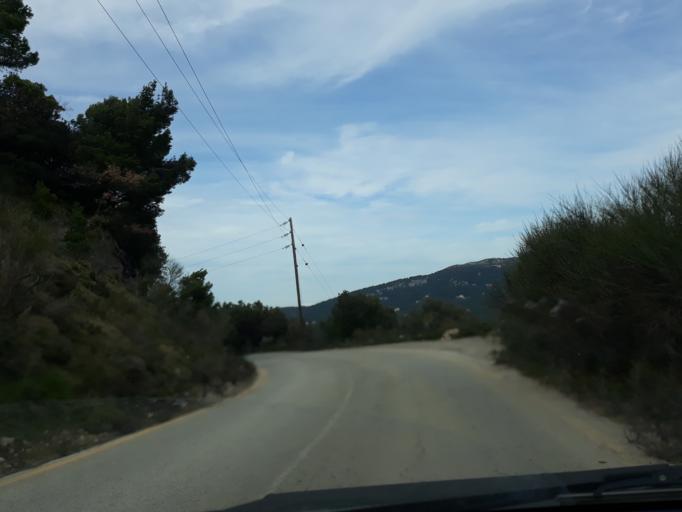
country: GR
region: Attica
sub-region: Nomarchia Anatolikis Attikis
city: Afidnes
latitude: 38.1845
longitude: 23.7930
